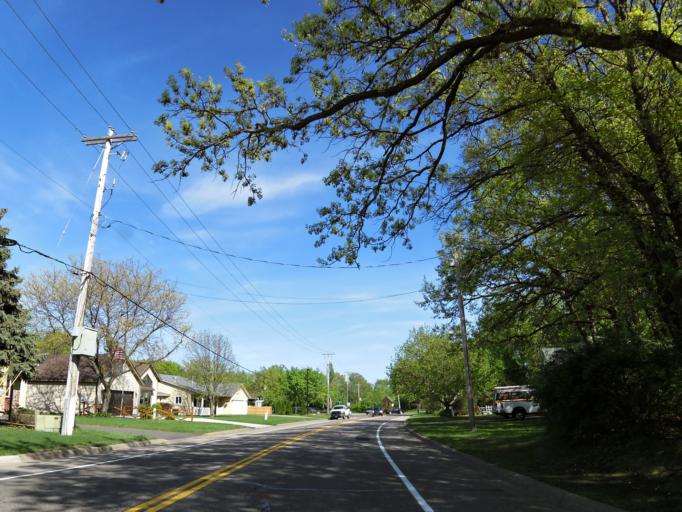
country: US
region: Minnesota
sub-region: Ramsey County
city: North Saint Paul
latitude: 45.0071
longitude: -92.9626
